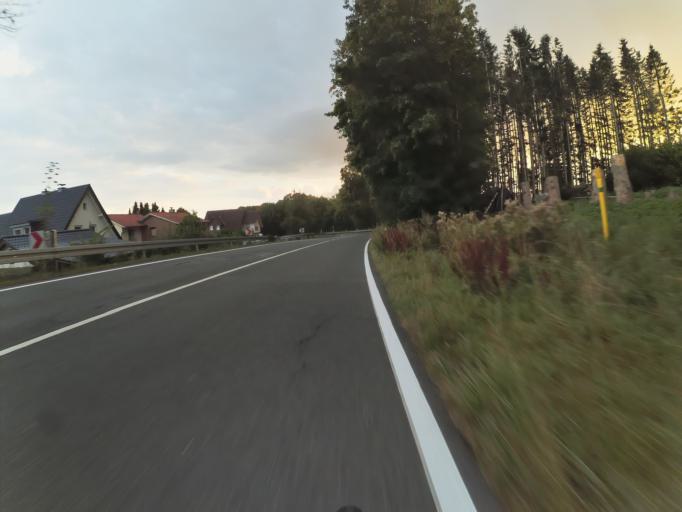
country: DE
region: North Rhine-Westphalia
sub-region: Regierungsbezirk Munster
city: Tecklenburg
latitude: 52.2759
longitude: 7.8270
